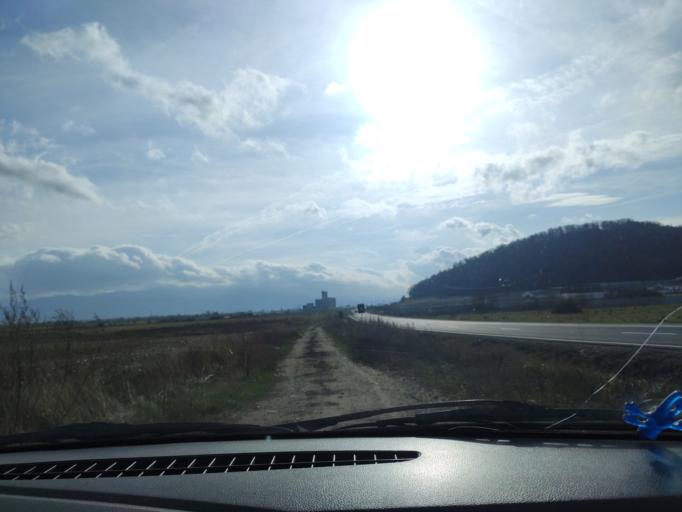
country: RO
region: Brasov
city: Codlea
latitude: 45.7218
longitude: 25.4535
